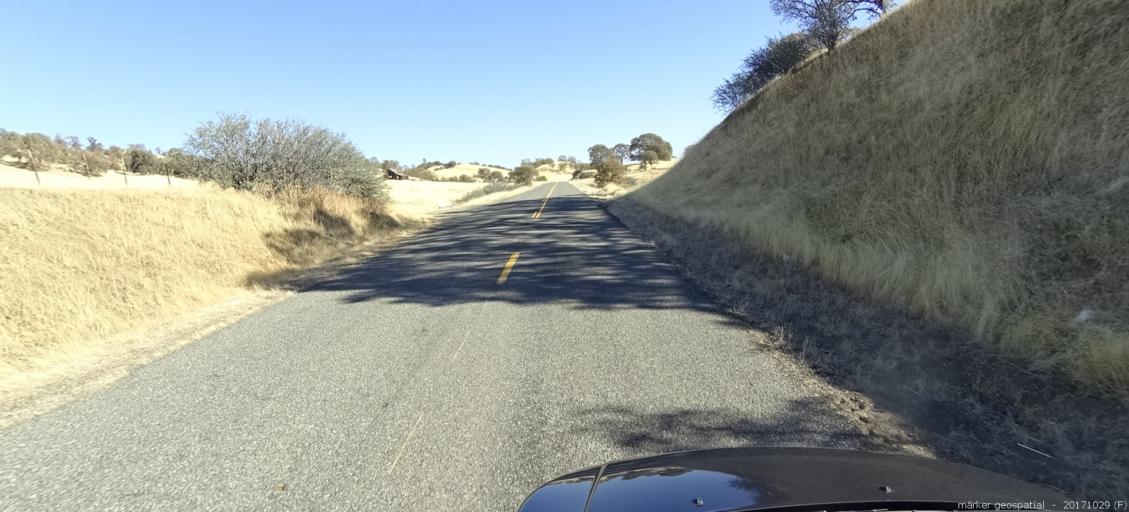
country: US
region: California
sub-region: Shasta County
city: Shasta
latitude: 40.4421
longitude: -122.6564
